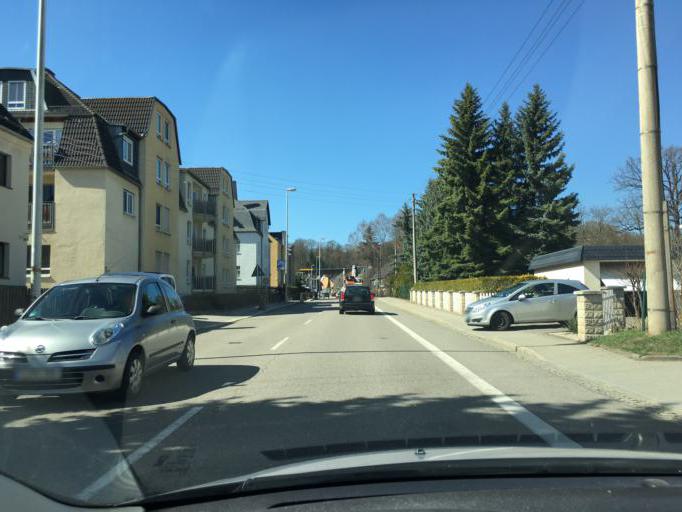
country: DE
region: Saxony
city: Neukirchen
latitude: 50.8293
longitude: 12.8248
